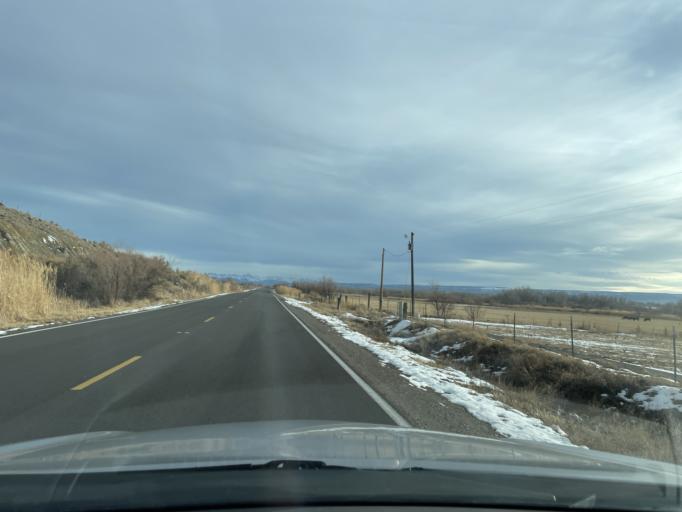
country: US
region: Colorado
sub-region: Montrose County
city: Olathe
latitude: 38.6538
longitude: -107.9966
